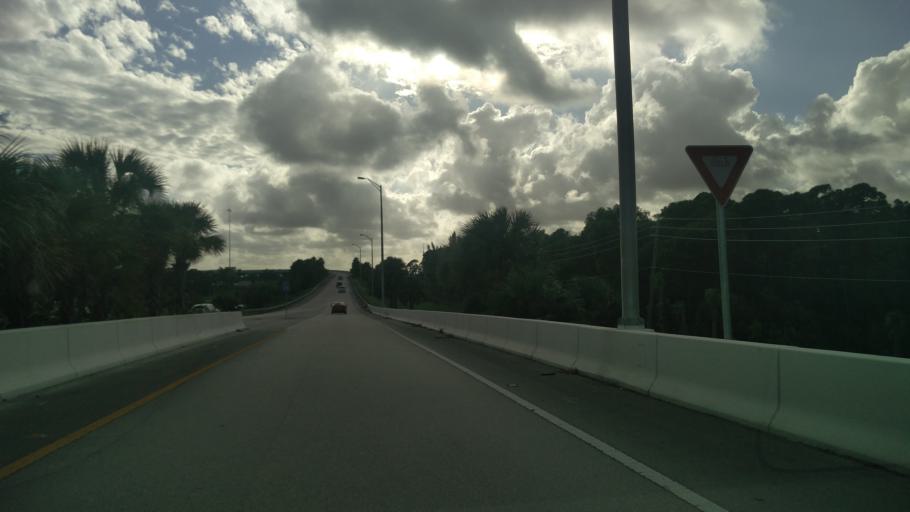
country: US
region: Florida
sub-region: Palm Beach County
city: North Palm Beach
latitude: 26.8435
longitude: -80.0982
